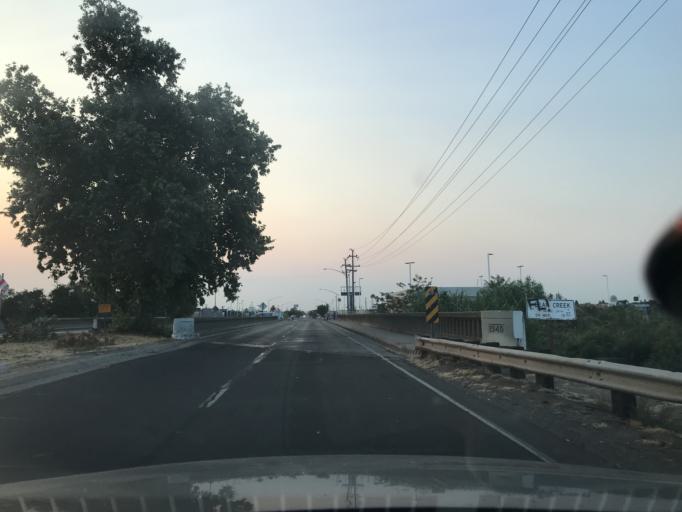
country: US
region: California
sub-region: Merced County
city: Merced
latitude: 37.3079
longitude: -120.5044
